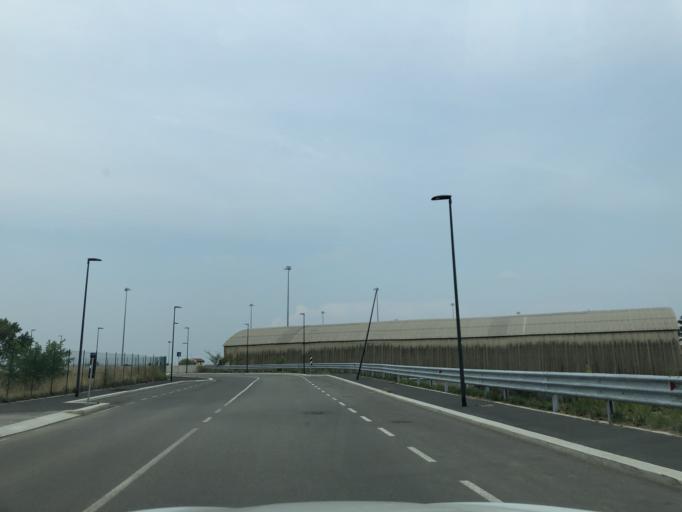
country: IT
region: Lombardy
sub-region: Citta metropolitana di Milano
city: Pero
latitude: 45.5098
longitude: 9.1052
